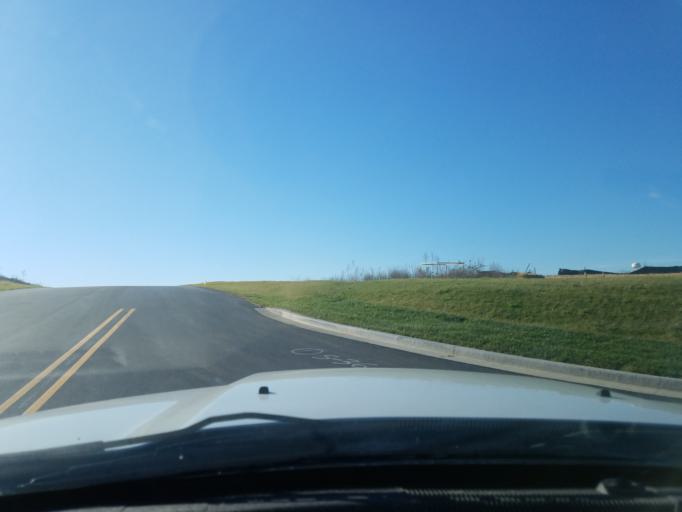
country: US
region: Indiana
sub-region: Clark County
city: Oak Park
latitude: 38.3649
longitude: -85.6817
